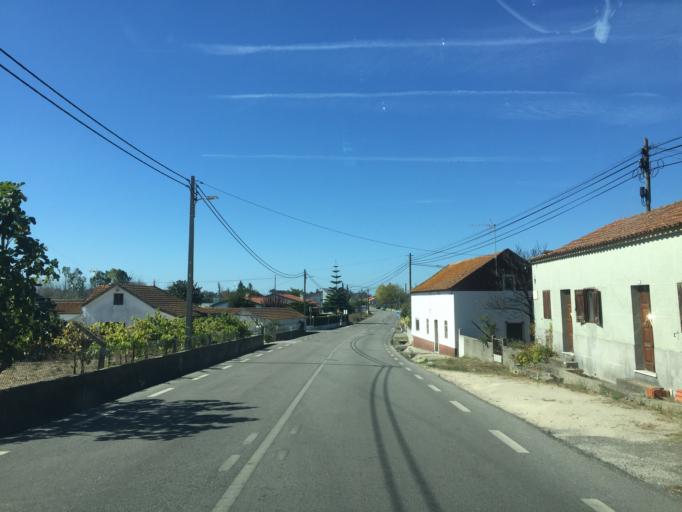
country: PT
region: Coimbra
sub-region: Mira
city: Mira
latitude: 40.3190
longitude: -8.7679
